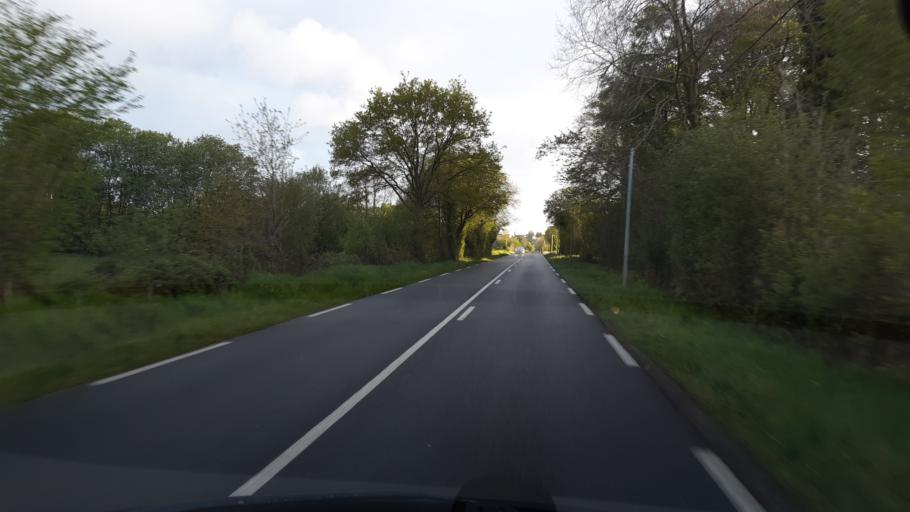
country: FR
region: Lower Normandy
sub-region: Departement de la Manche
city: Tessy-sur-Vire
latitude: 49.0155
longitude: -1.1486
